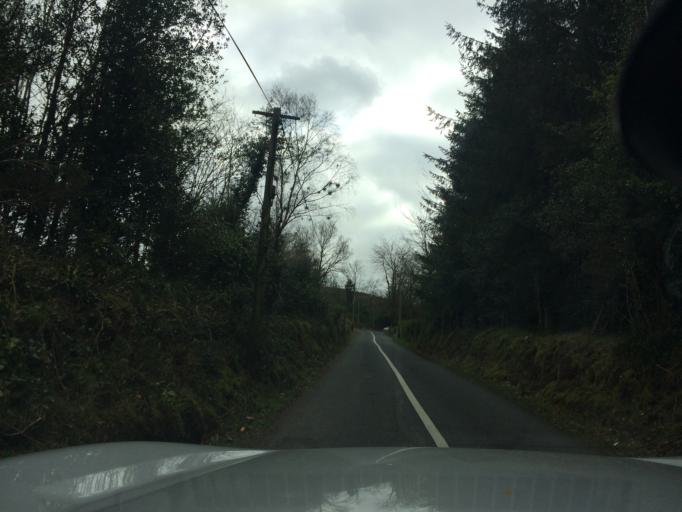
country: IE
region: Munster
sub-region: South Tipperary
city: Cluain Meala
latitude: 52.3444
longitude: -7.6375
